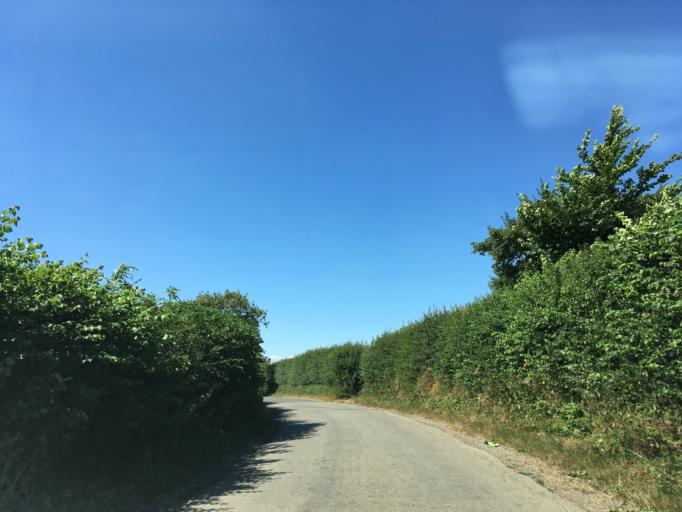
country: GB
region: England
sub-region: South Gloucestershire
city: Hinton
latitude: 51.5121
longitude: -2.3927
